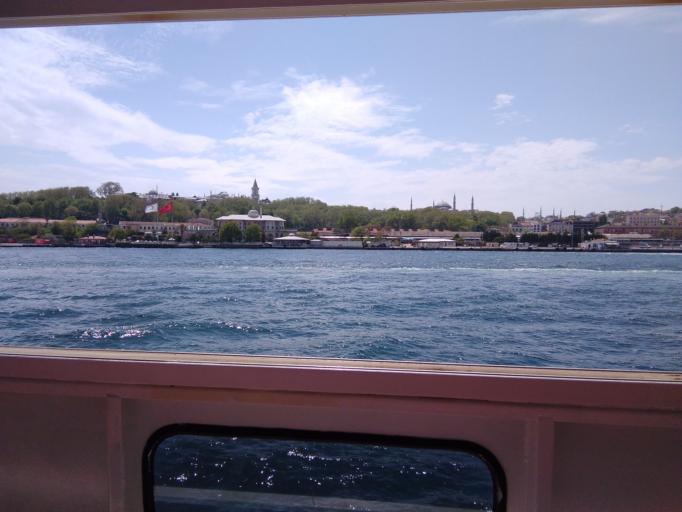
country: TR
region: Istanbul
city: Eminoenue
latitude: 41.0196
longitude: 28.9802
